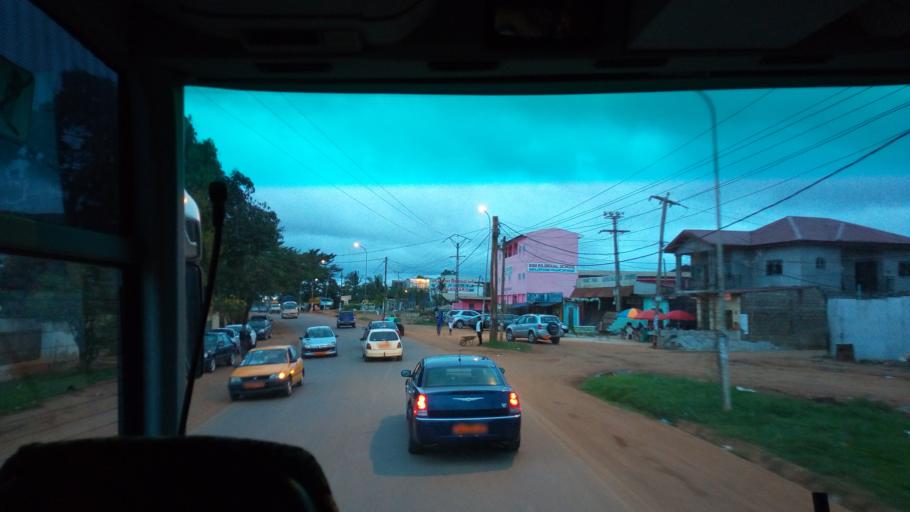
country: CM
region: Centre
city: Yaounde
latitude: 3.7920
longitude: 11.5225
